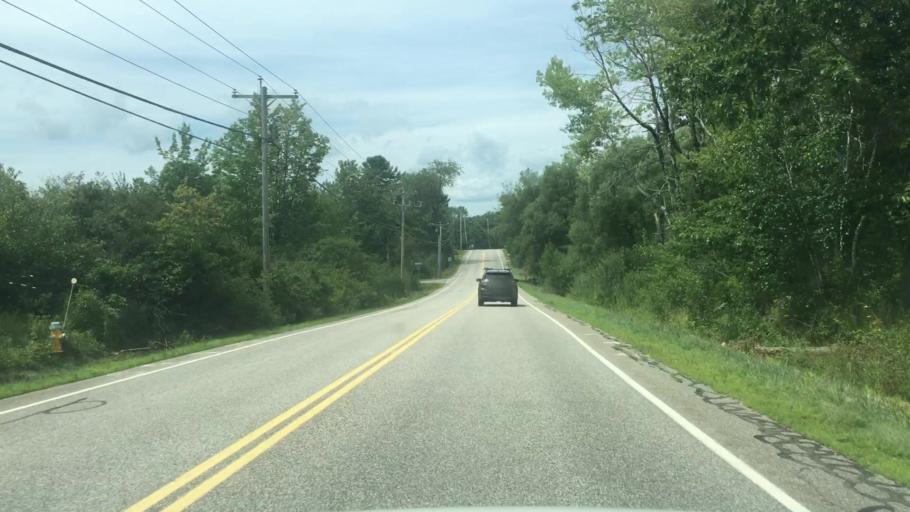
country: US
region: Maine
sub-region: Cumberland County
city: Scarborough
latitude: 43.5798
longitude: -70.2888
